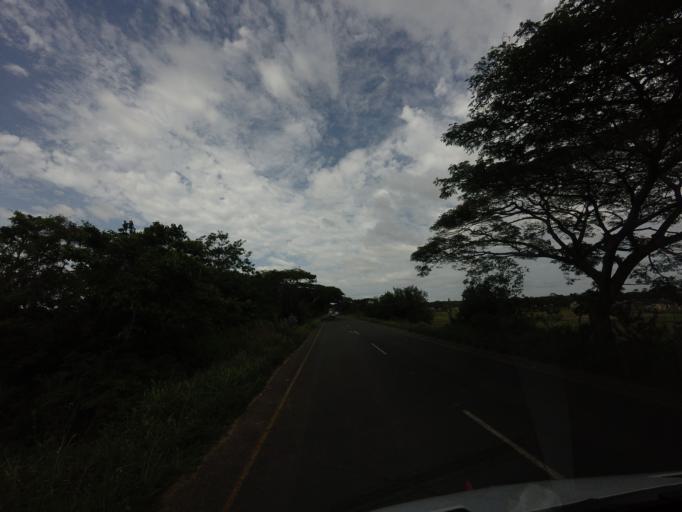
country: ZA
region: KwaZulu-Natal
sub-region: uMkhanyakude District Municipality
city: Mtubatuba
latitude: -28.3832
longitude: 32.3547
